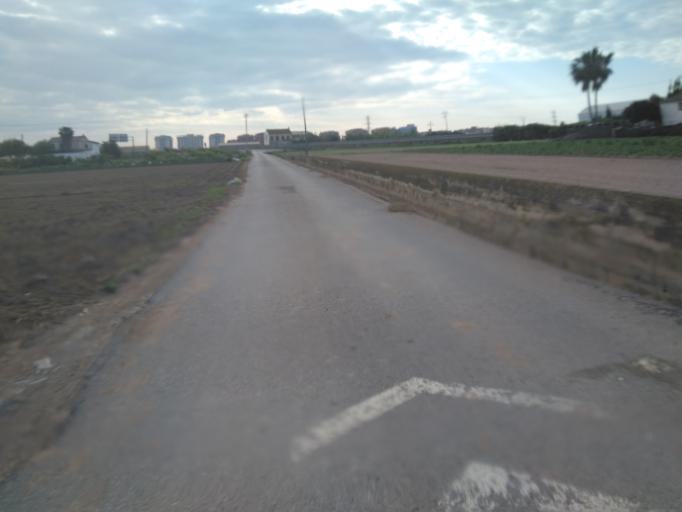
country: ES
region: Valencia
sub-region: Provincia de Valencia
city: Alboraya
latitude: 39.4907
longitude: -0.3403
